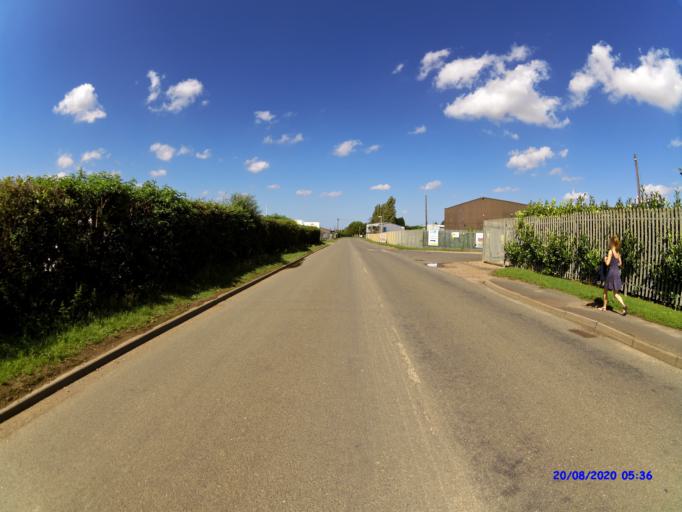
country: GB
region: England
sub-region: Cambridgeshire
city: Whittlesey
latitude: 52.5470
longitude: -0.1166
